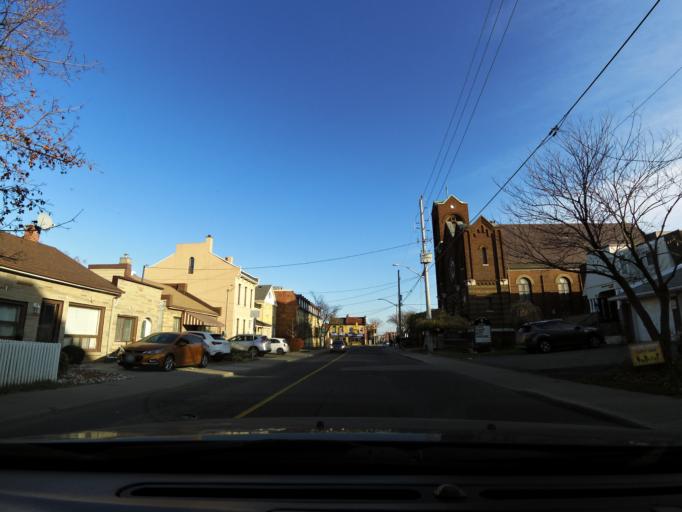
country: CA
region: Ontario
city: Hamilton
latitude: 43.2645
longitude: -79.8670
